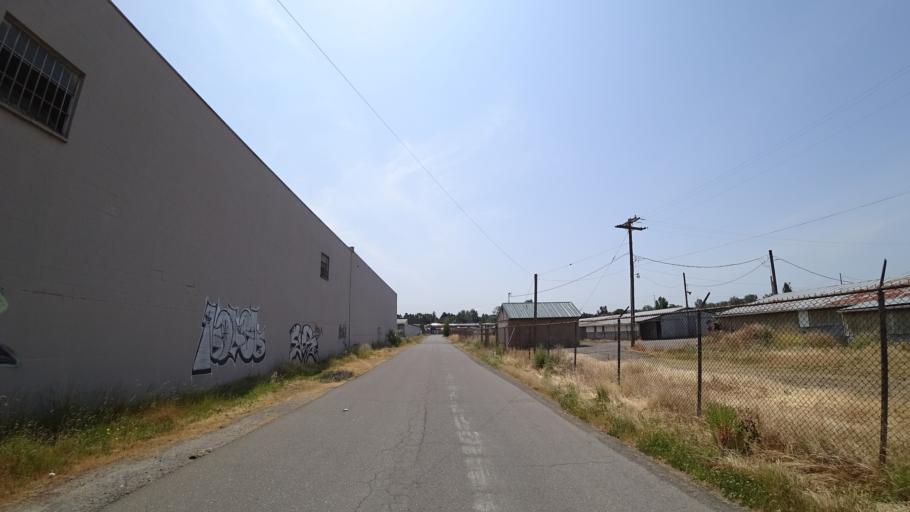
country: US
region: Washington
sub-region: Clark County
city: Vancouver
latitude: 45.5900
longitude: -122.6690
